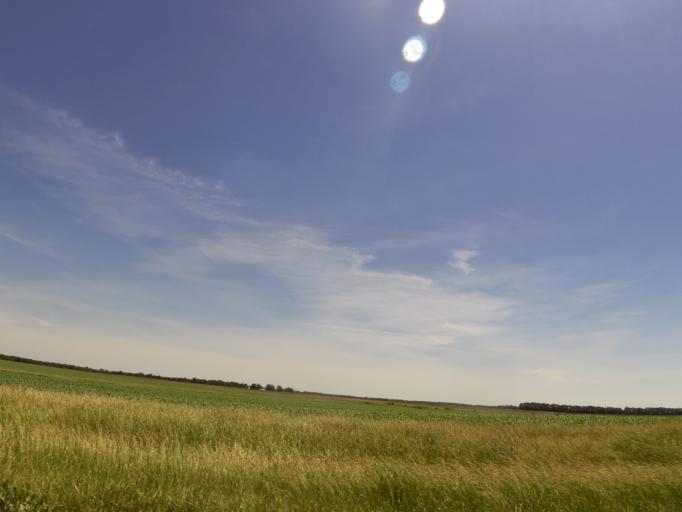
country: US
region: Illinois
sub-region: Vermilion County
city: Rossville
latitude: 40.3017
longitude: -87.6581
